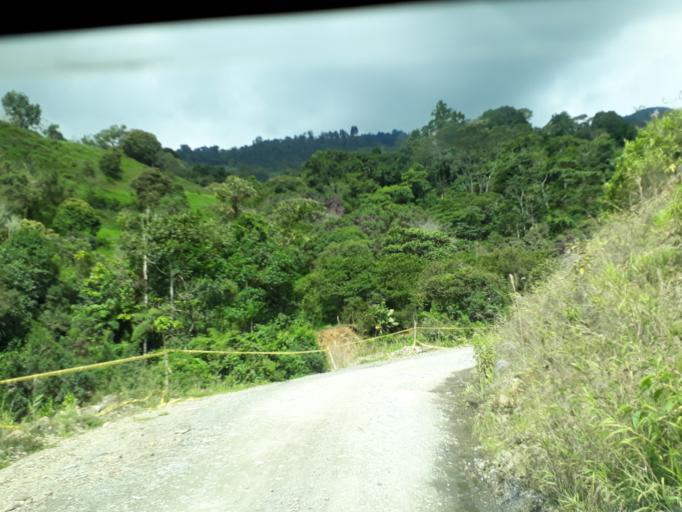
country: CO
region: Cundinamarca
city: Pacho
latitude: 5.2579
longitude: -74.1896
